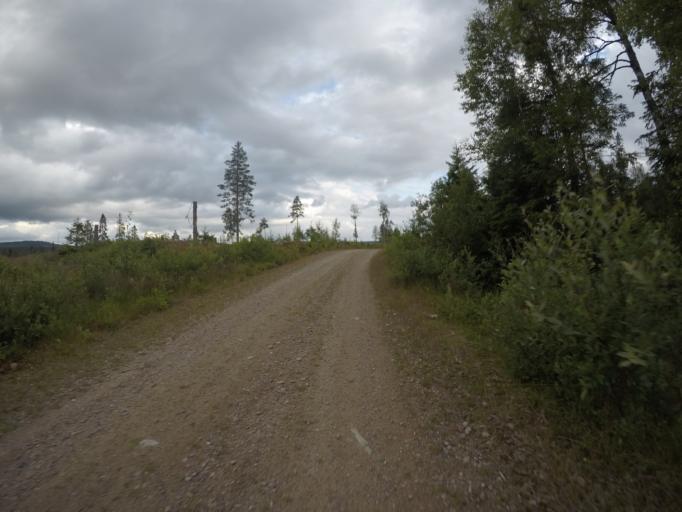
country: SE
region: Vaermland
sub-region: Filipstads Kommun
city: Lesjofors
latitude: 60.1625
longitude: 14.4013
